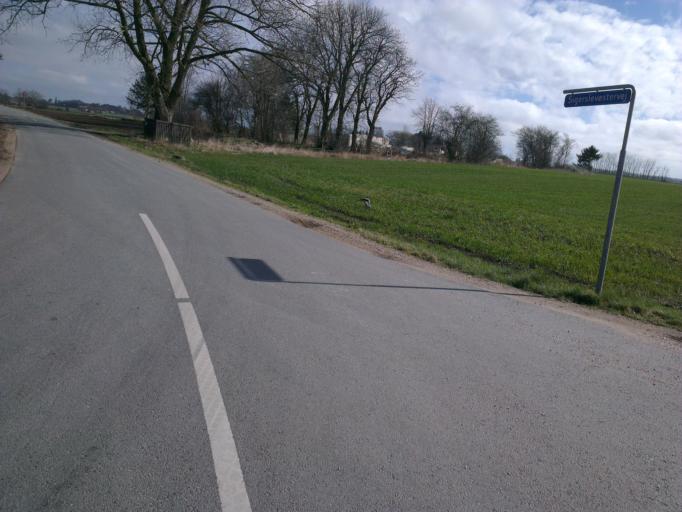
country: DK
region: Capital Region
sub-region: Frederikssund Kommune
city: Frederikssund
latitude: 55.8594
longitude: 12.1035
